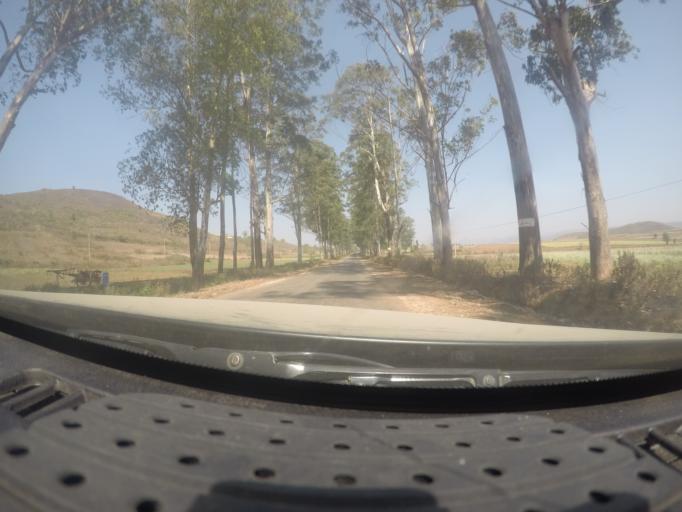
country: MM
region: Shan
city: Taunggyi
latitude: 20.8491
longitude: 96.5938
